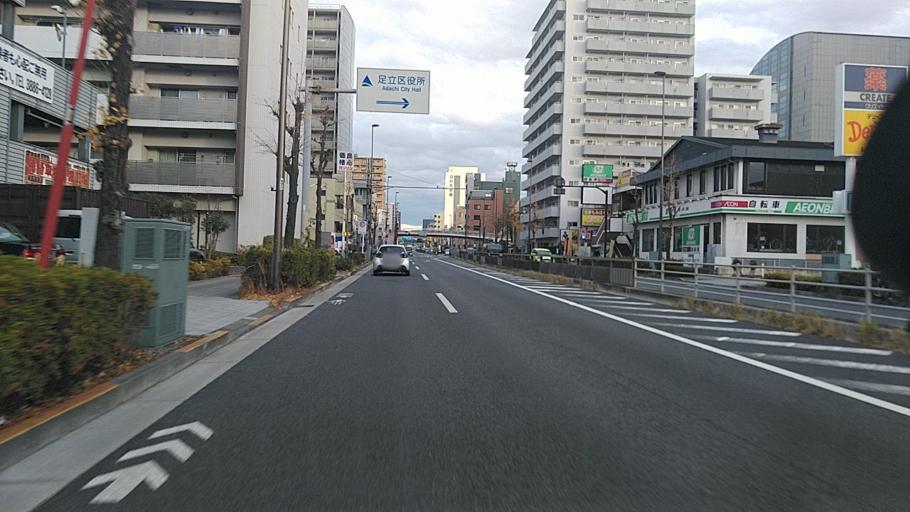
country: JP
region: Saitama
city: Soka
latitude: 35.7738
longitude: 139.8033
